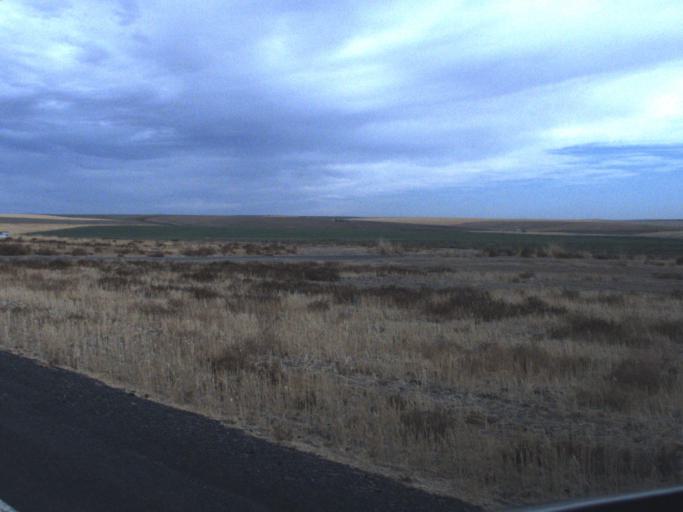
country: US
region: Washington
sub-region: Okanogan County
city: Coulee Dam
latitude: 47.4844
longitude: -118.7848
